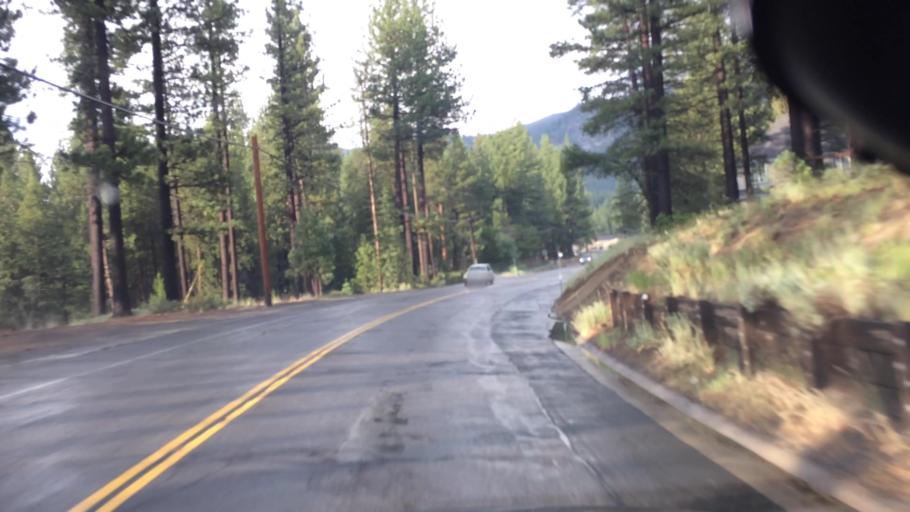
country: US
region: California
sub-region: El Dorado County
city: South Lake Tahoe
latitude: 38.9053
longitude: -119.9682
